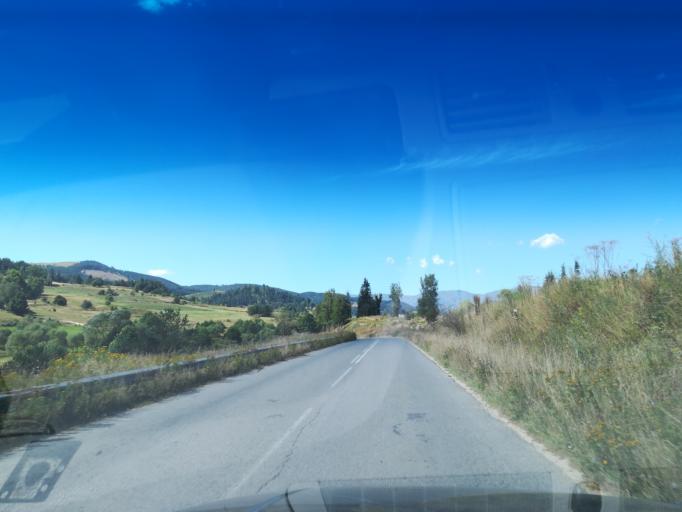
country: BG
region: Sofiya
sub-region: Obshtina Koprivshtitsa
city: Koprivshtitsa
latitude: 42.6118
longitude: 24.3750
